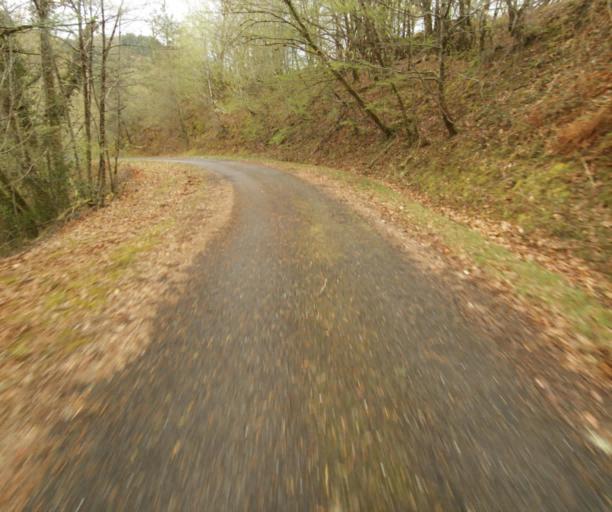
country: FR
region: Limousin
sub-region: Departement de la Correze
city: Saint-Privat
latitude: 45.2070
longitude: 2.0321
